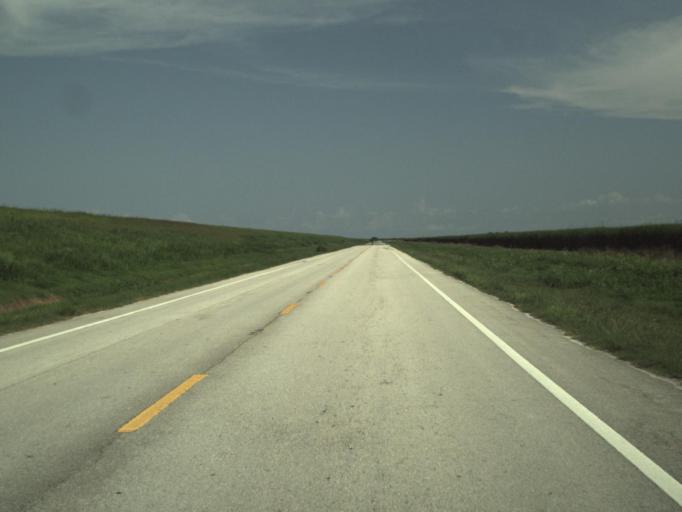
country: US
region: Florida
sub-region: Palm Beach County
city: Pahokee
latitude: 26.7548
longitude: -80.6839
